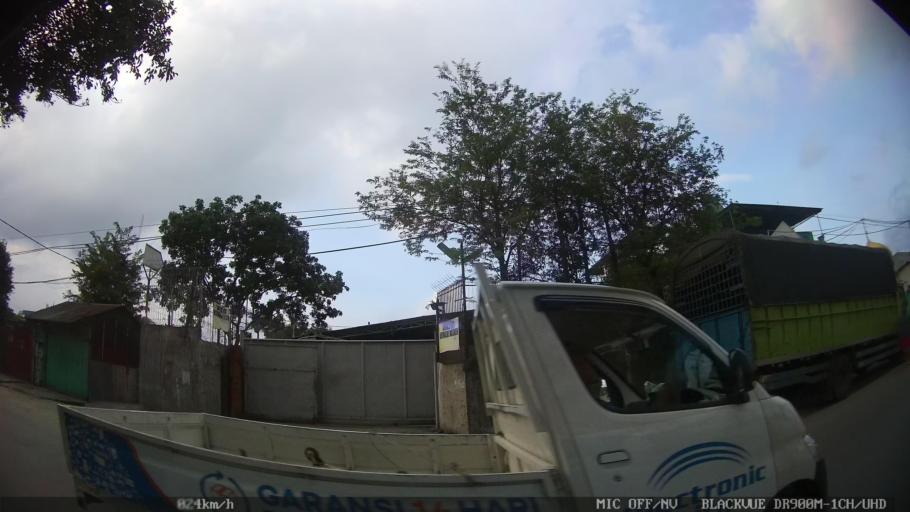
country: ID
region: North Sumatra
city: Medan
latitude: 3.5974
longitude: 98.7308
